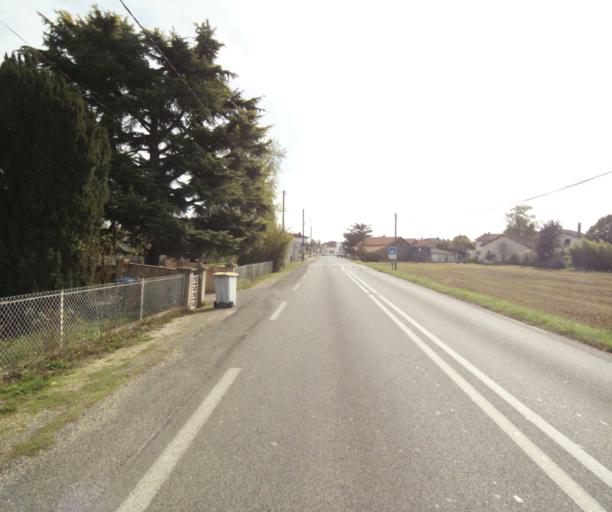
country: FR
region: Midi-Pyrenees
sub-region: Departement du Tarn-et-Garonne
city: Orgueil
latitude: 43.9195
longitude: 1.3970
